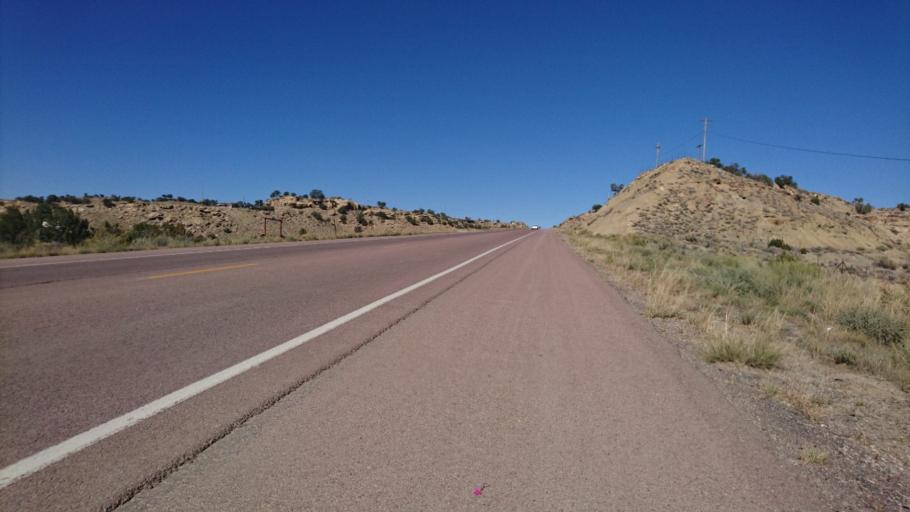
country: US
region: New Mexico
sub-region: McKinley County
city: Gallup
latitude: 35.4720
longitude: -108.7423
